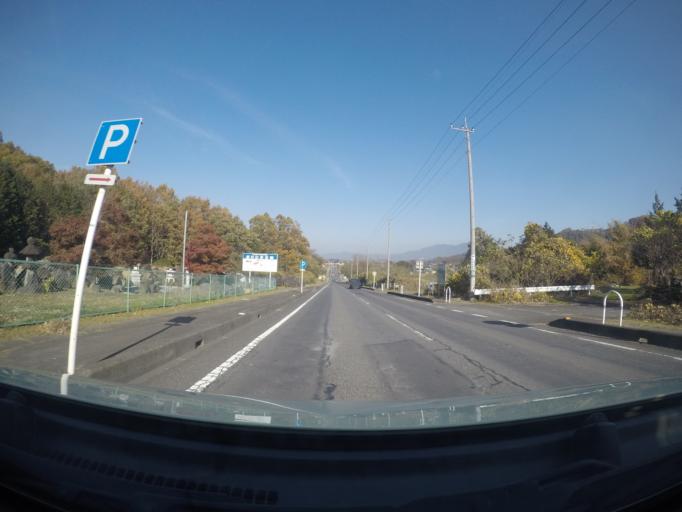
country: JP
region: Ibaraki
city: Makabe
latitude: 36.2431
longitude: 140.0672
